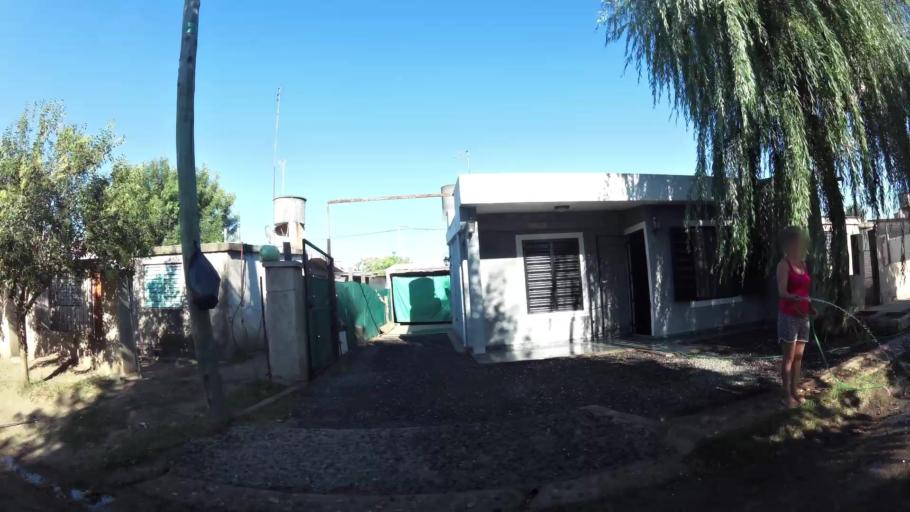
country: AR
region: Cordoba
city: Villa Allende
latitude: -31.3315
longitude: -64.2410
